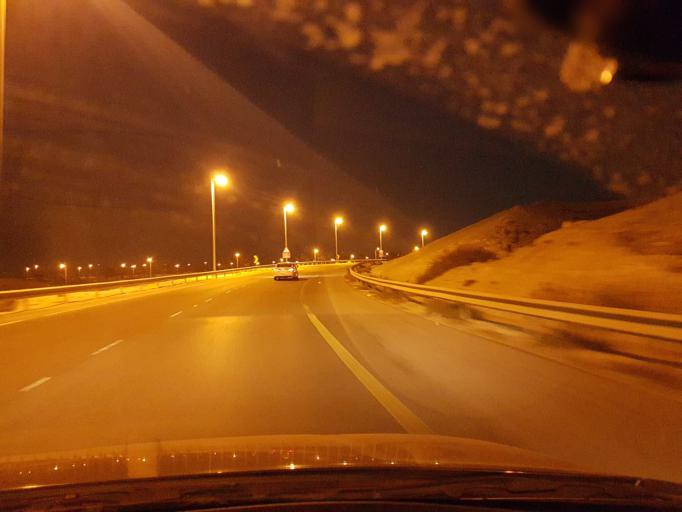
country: BH
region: Central Governorate
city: Dar Kulayb
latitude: 26.0583
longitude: 50.5145
